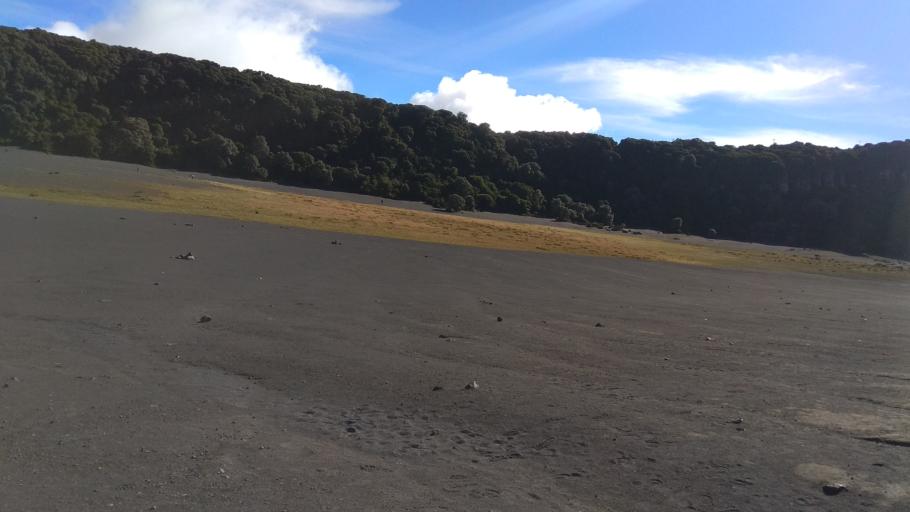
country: CR
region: Cartago
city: Cot
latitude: 9.9794
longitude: -83.8479
